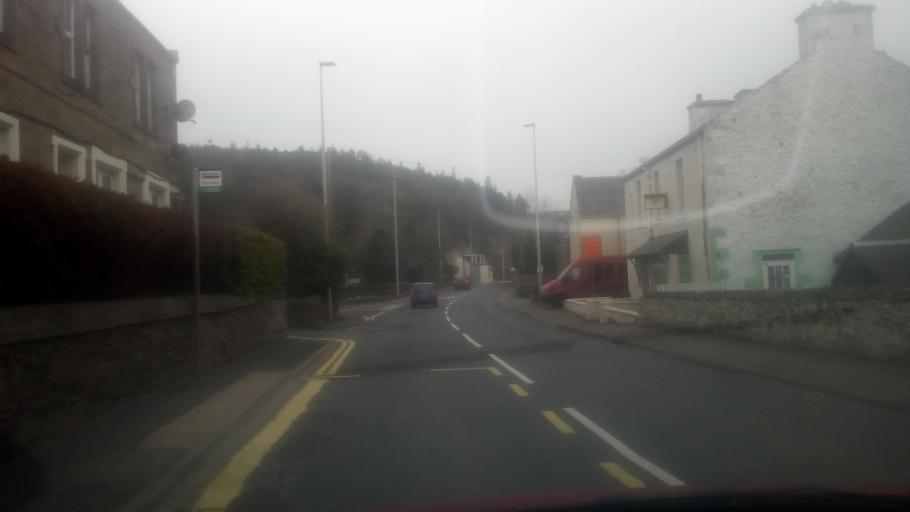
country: GB
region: Scotland
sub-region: The Scottish Borders
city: Galashiels
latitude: 55.6965
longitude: -2.8661
